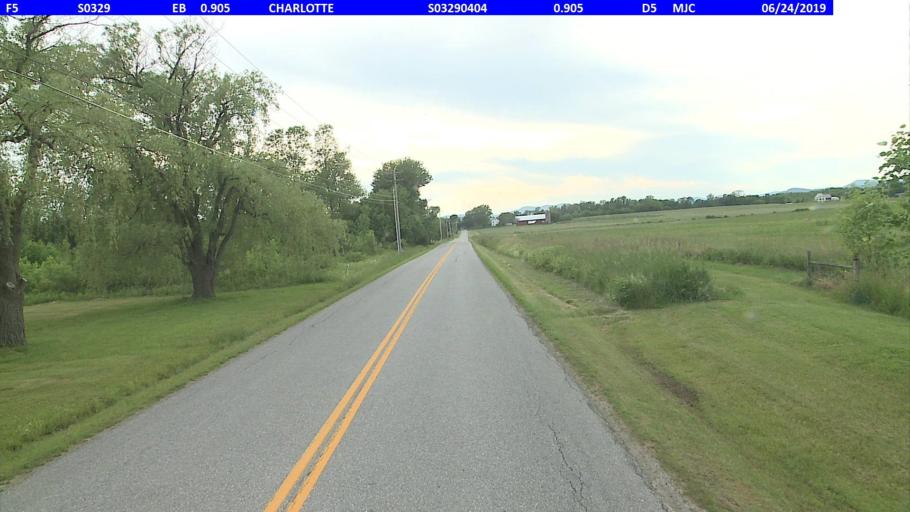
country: US
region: Vermont
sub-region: Addison County
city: Vergennes
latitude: 44.3094
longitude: -73.2640
